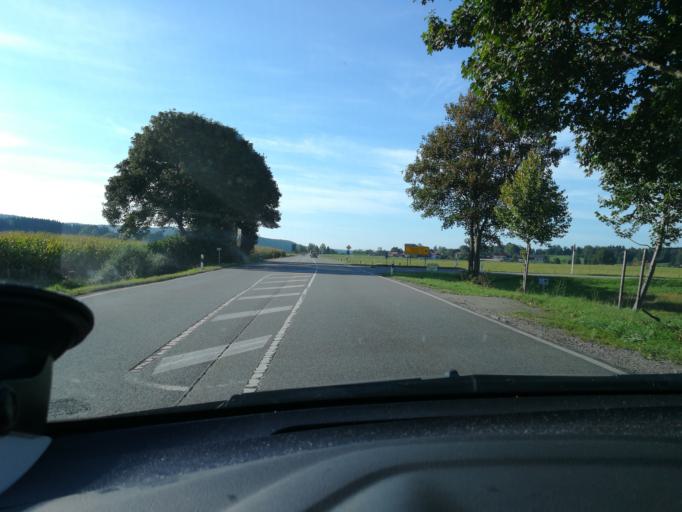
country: DE
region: Bavaria
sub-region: Upper Bavaria
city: Miesbach
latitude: 47.8218
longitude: 11.8338
